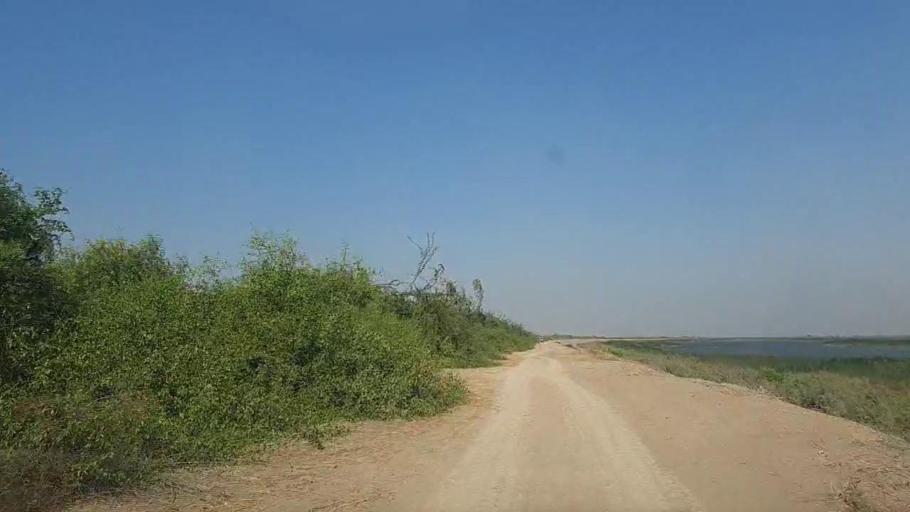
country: PK
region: Sindh
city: Daro Mehar
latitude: 24.9188
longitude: 68.0784
